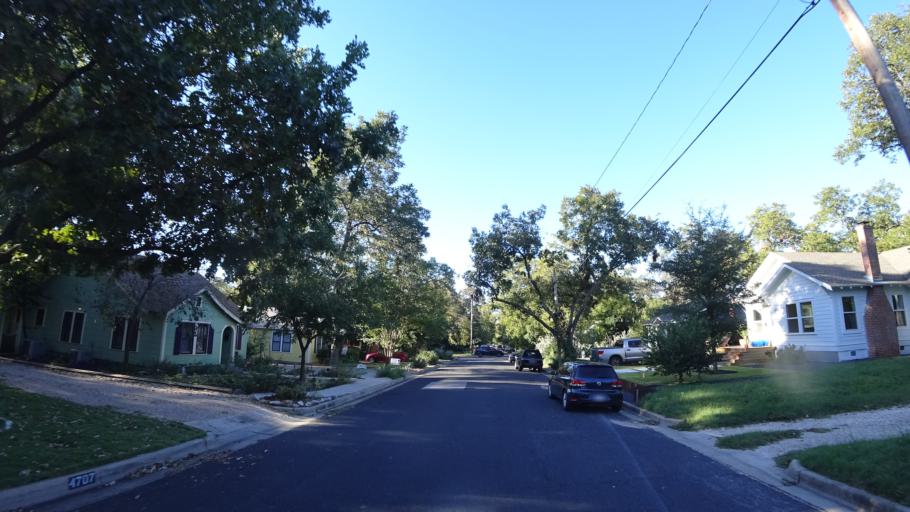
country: US
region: Texas
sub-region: Travis County
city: Austin
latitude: 30.3106
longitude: -97.7234
